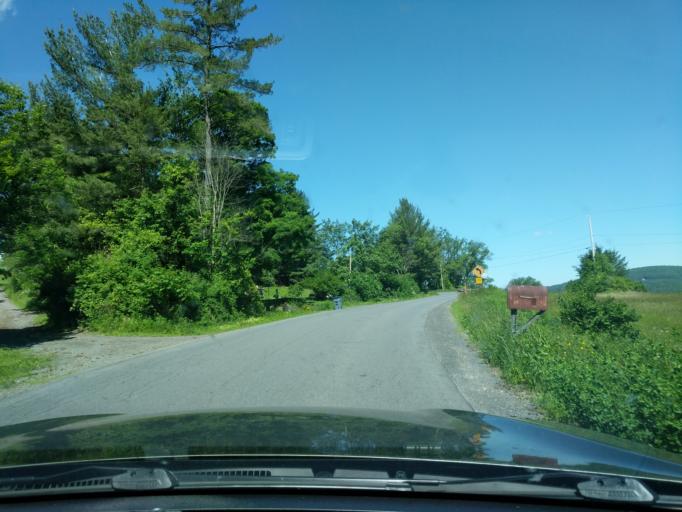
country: US
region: New York
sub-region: Tompkins County
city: Dryden
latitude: 42.3793
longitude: -76.3601
